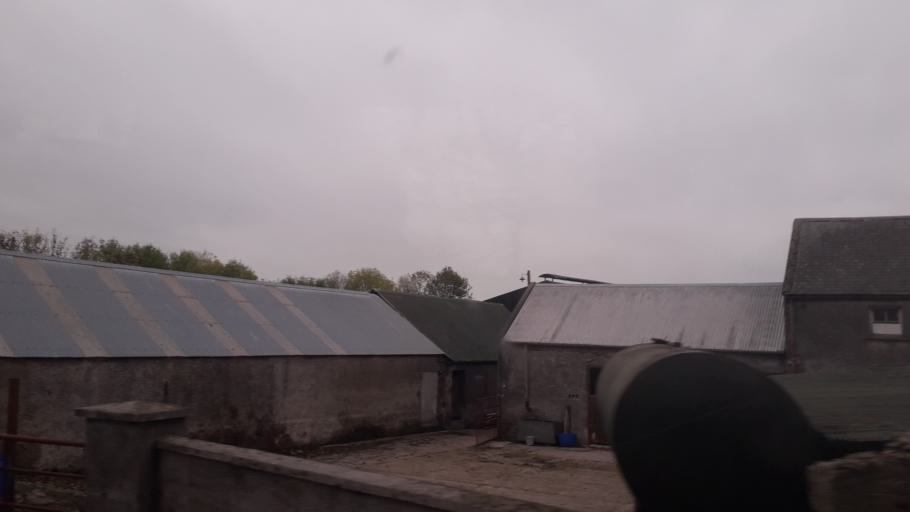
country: IE
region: Leinster
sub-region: Uibh Fhaili
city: Birr
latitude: 52.9681
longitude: -8.0052
